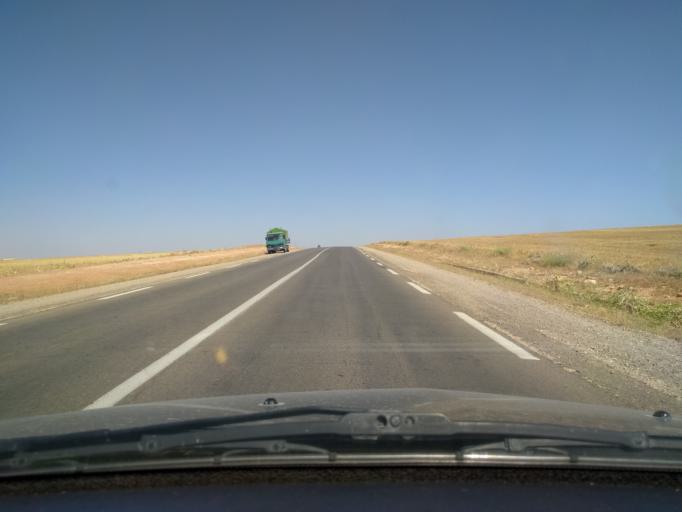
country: DZ
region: Tiaret
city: Frenda
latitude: 34.8840
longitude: 1.1891
